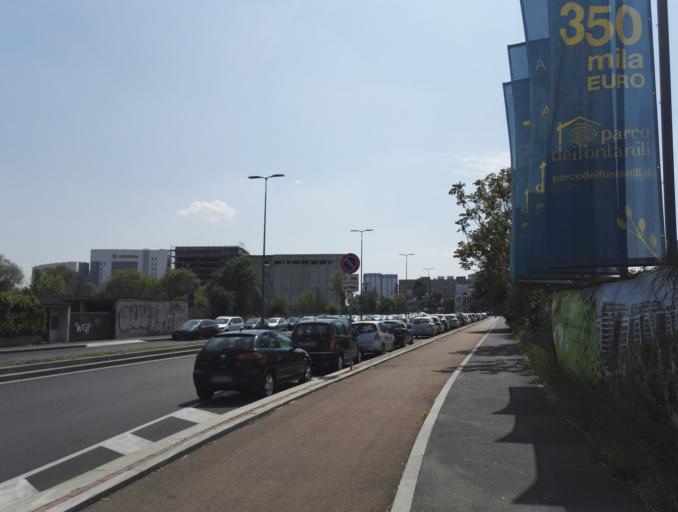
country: IT
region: Lombardy
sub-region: Citta metropolitana di Milano
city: Romano Banco
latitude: 45.4509
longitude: 9.1186
